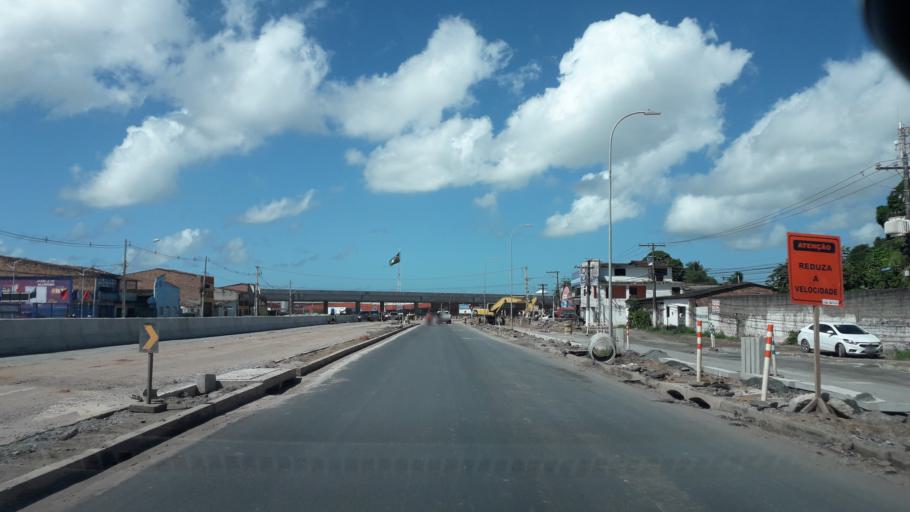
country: BR
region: Alagoas
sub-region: Satuba
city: Satuba
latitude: -9.5660
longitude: -35.7797
